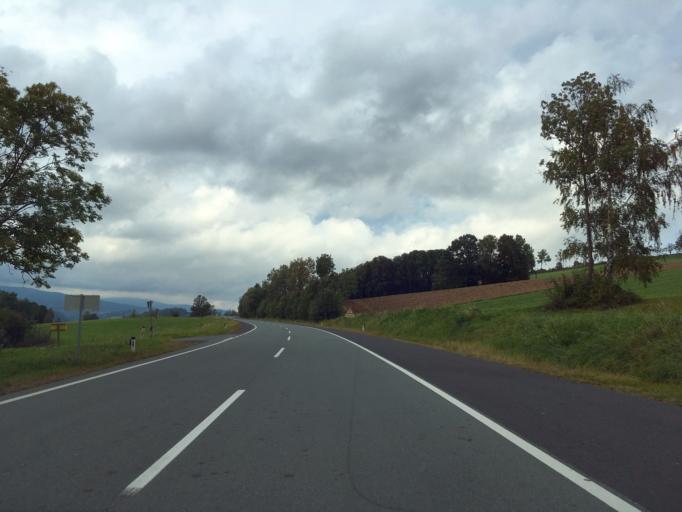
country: AT
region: Styria
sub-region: Politischer Bezirk Hartberg-Fuerstenfeld
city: Pinggau
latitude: 47.4398
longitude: 16.0788
